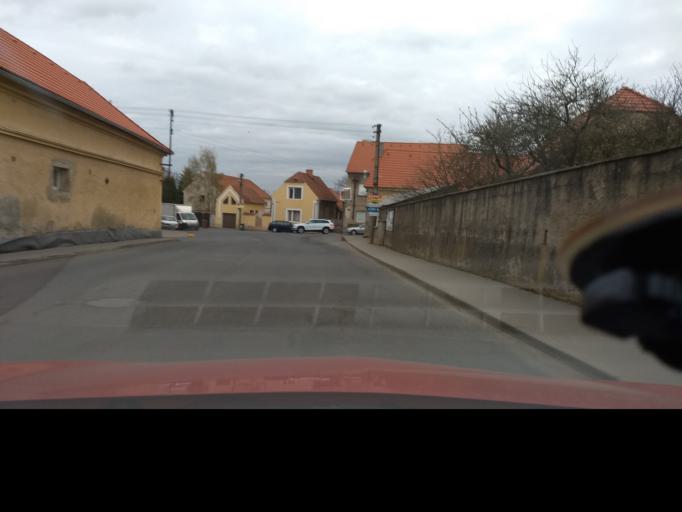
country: CZ
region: Central Bohemia
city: Unhost'
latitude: 50.0691
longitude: 14.1652
